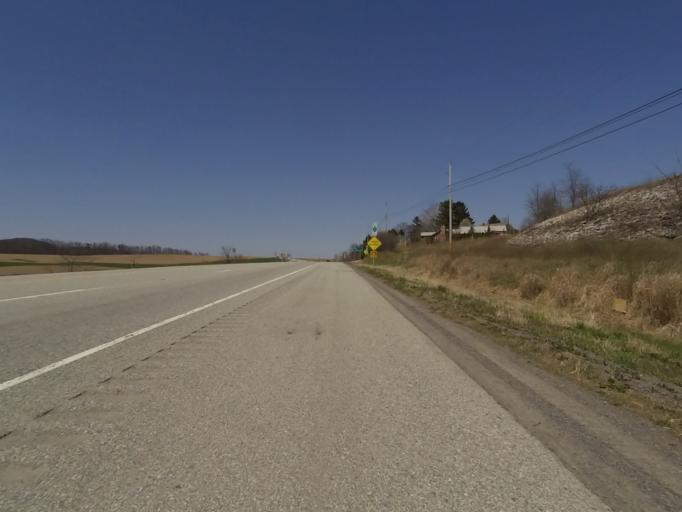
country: US
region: Pennsylvania
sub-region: Blair County
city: Williamsburg
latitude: 40.5795
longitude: -78.1427
